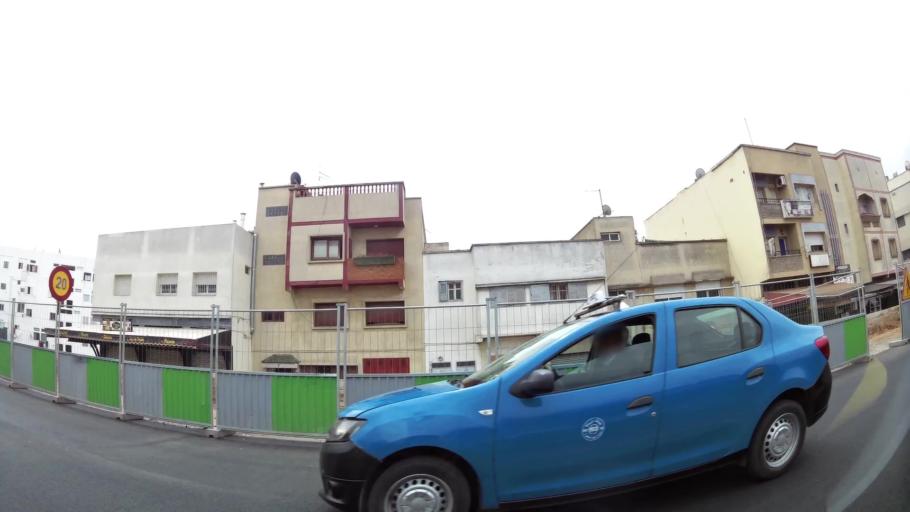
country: MA
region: Rabat-Sale-Zemmour-Zaer
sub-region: Rabat
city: Rabat
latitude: 33.9979
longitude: -6.8699
